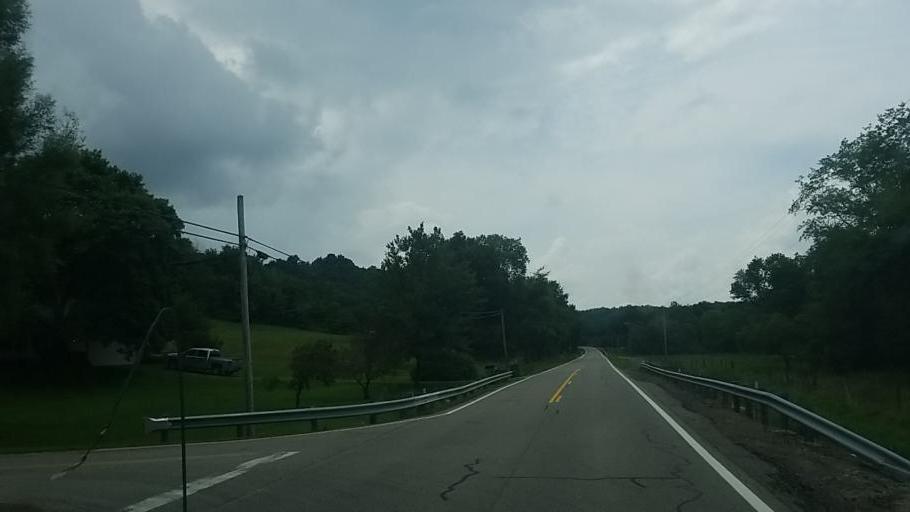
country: US
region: Ohio
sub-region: Muskingum County
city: Frazeysburg
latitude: 40.1774
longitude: -82.2681
